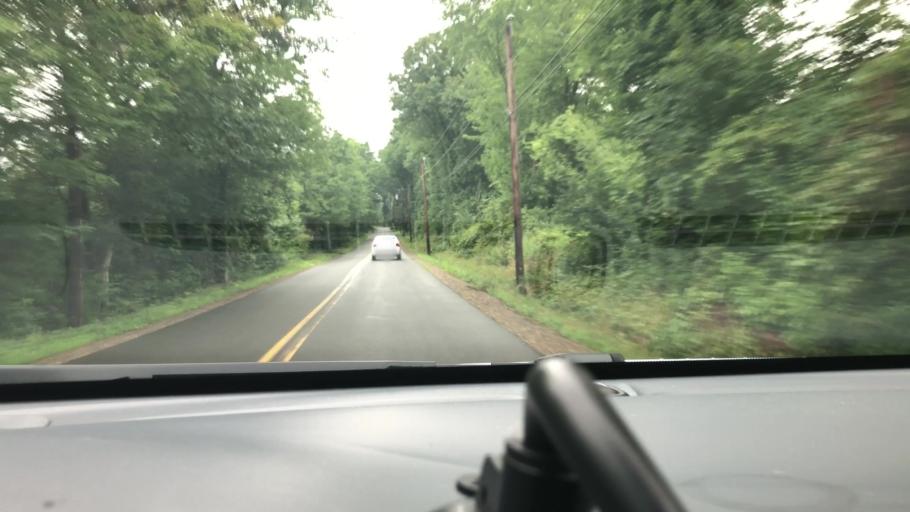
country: US
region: New Hampshire
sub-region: Hillsborough County
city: Pinardville
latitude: 42.9851
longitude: -71.5192
